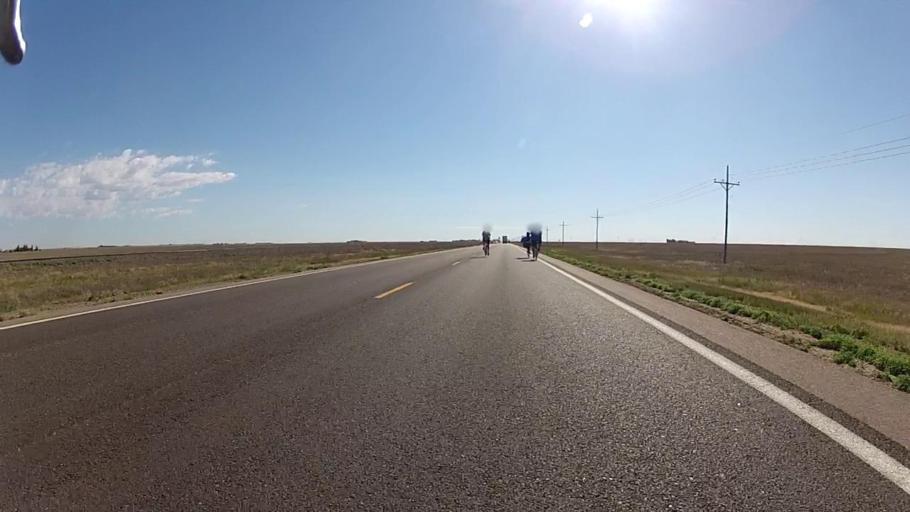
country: US
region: Kansas
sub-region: Gray County
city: Cimarron
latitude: 37.5816
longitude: -100.5057
